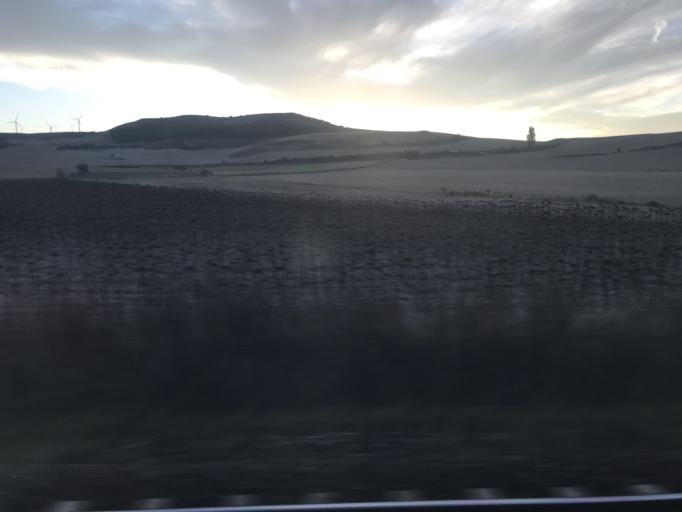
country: ES
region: Castille and Leon
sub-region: Provincia de Burgos
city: Santa Maria del Invierno
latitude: 42.4518
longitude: -3.4520
